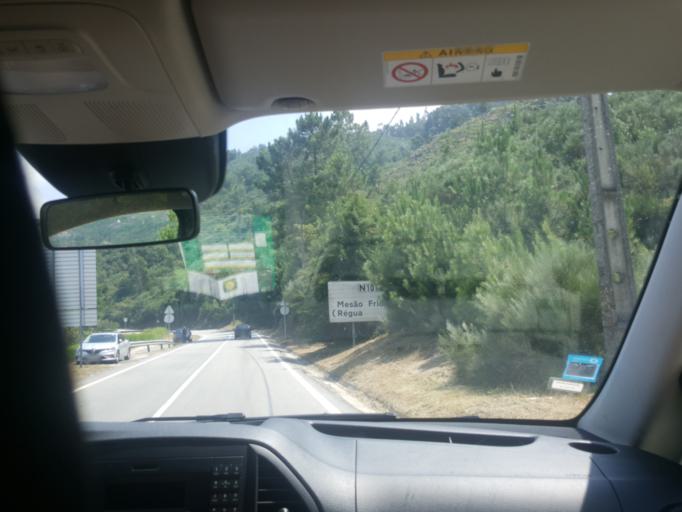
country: PT
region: Porto
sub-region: Amarante
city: Amarante
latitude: 41.2435
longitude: -8.0338
